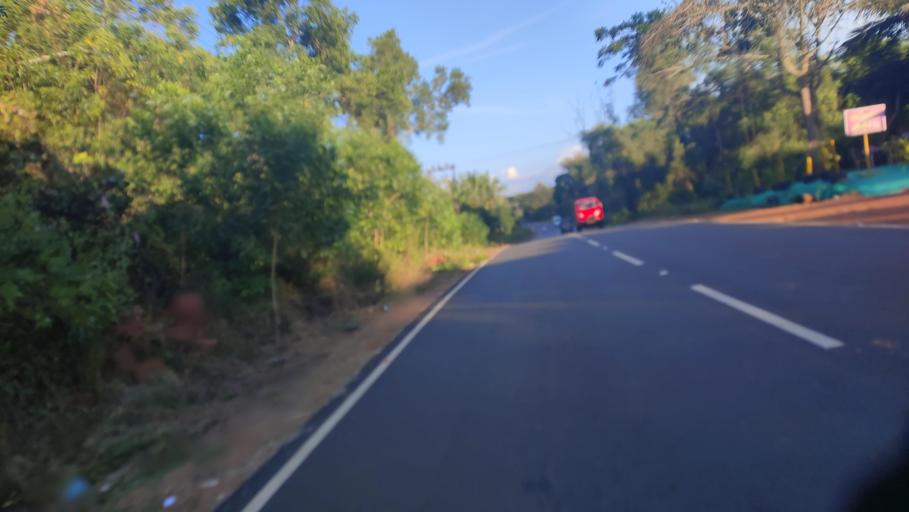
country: IN
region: Kerala
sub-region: Kasaragod District
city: Kasaragod
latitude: 12.4579
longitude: 75.0922
